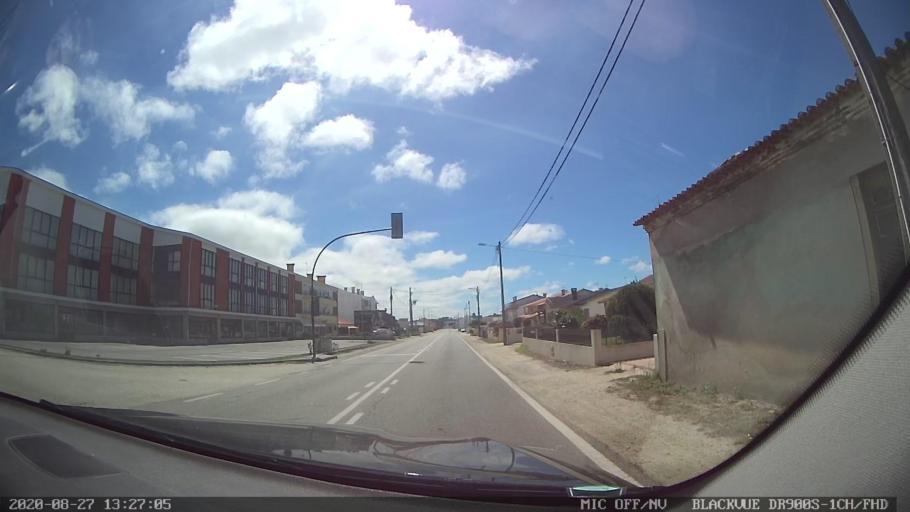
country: PT
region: Aveiro
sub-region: Vagos
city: Vagos
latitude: 40.5333
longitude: -8.6778
